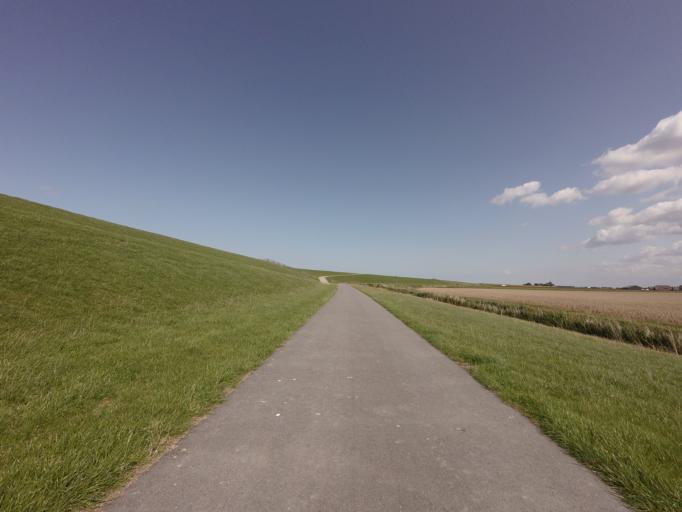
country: NL
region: Friesland
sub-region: Gemeente Dongeradeel
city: Holwerd
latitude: 53.3757
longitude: 5.8777
